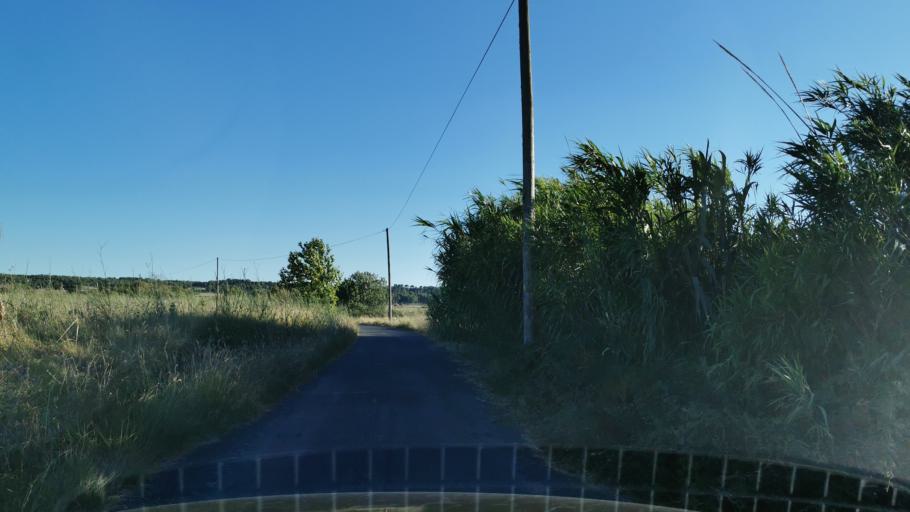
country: FR
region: Languedoc-Roussillon
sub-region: Departement de l'Aude
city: Ouveillan
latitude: 43.2834
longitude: 2.9761
